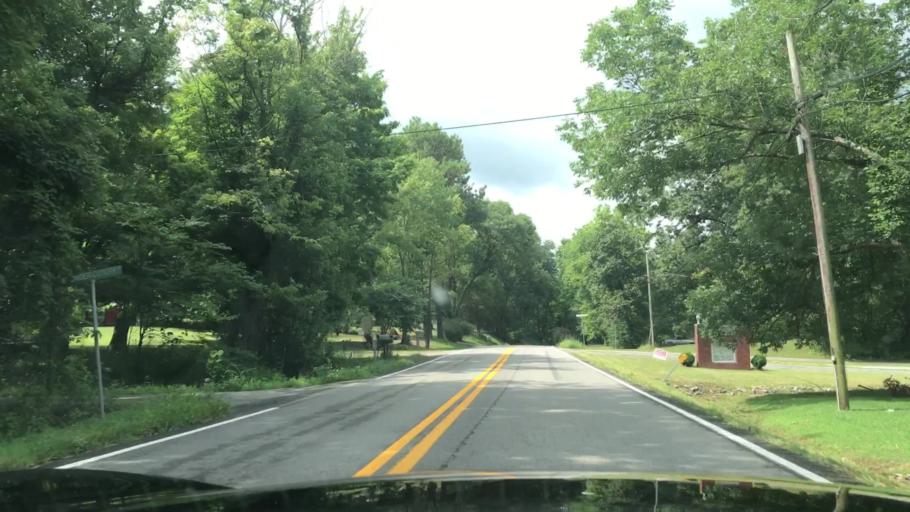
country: US
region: Kentucky
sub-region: Muhlenberg County
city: Central City
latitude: 37.1998
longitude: -87.0296
